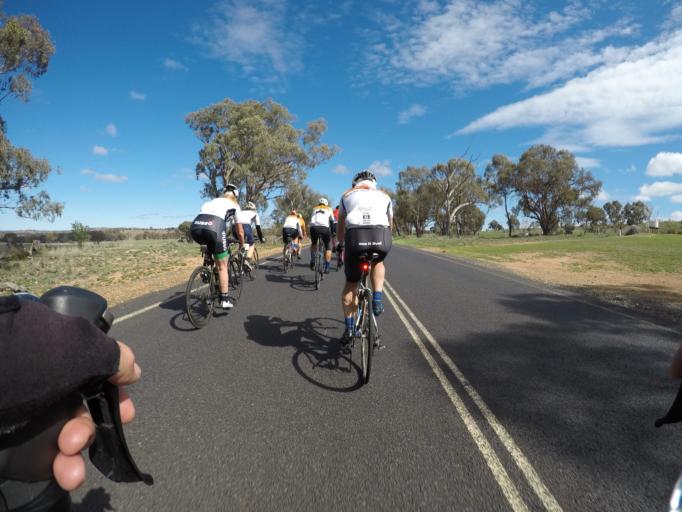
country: AU
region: New South Wales
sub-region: Parkes
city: Peak Hill
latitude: -32.7378
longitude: 148.5790
